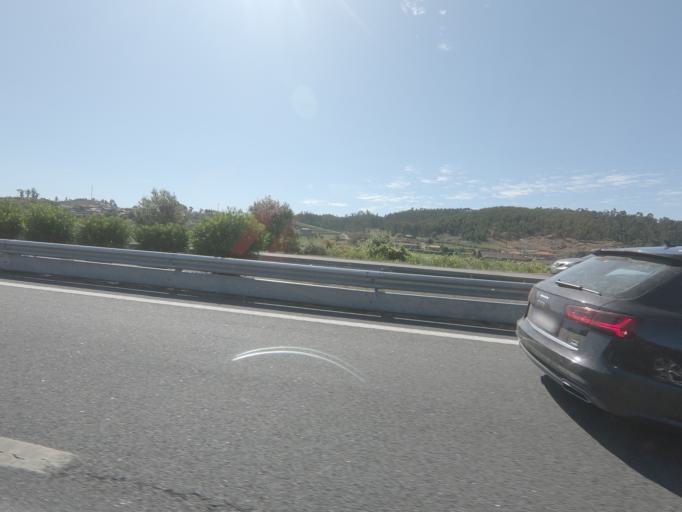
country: PT
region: Porto
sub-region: Lousada
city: Meinedo
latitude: 41.2208
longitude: -8.2397
